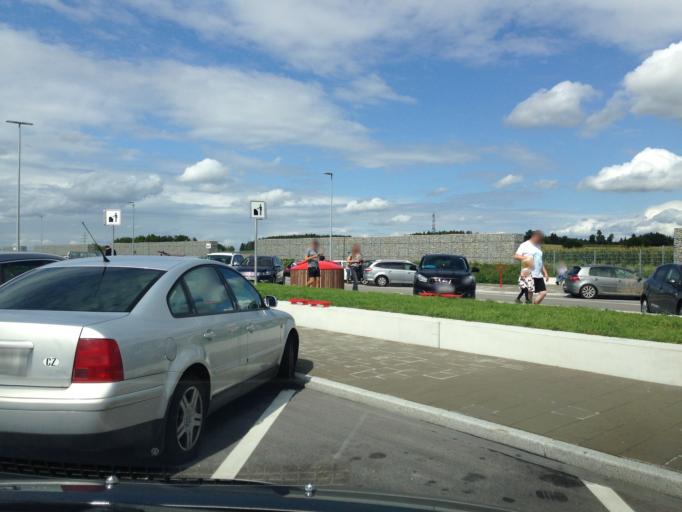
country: DE
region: Bavaria
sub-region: Upper Bavaria
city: Eching
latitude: 48.3374
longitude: 11.6109
